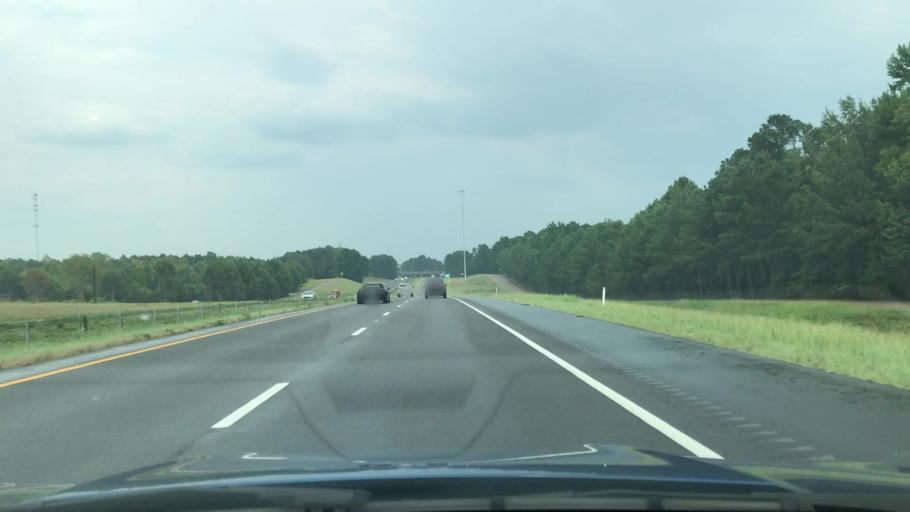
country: US
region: Texas
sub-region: Harrison County
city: Hallsville
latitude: 32.4861
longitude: -94.4786
